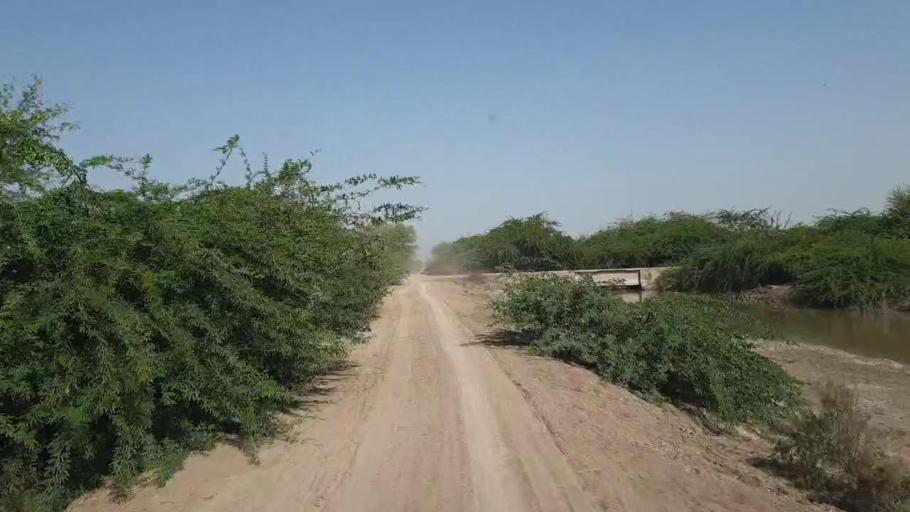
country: PK
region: Sindh
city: Tando Bago
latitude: 24.6736
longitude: 69.0684
